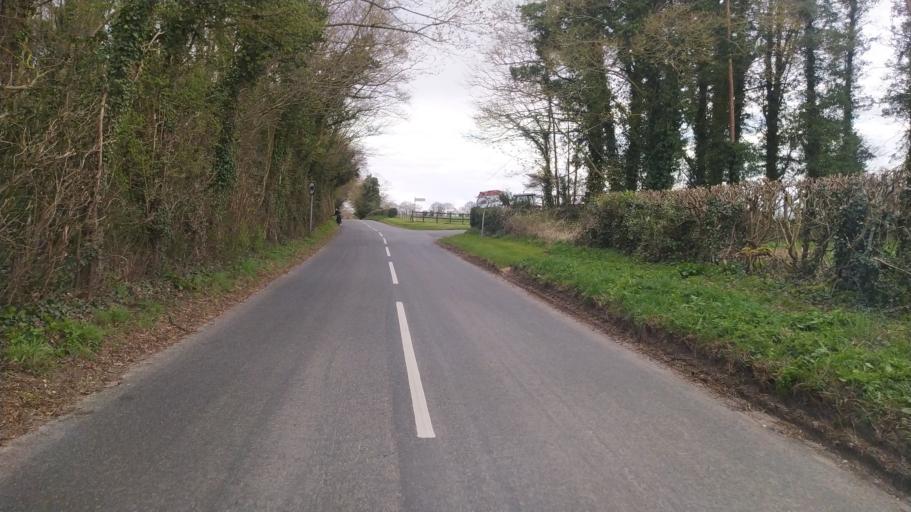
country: GB
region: England
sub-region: Hampshire
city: Kings Worthy
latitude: 51.1335
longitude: -1.3090
